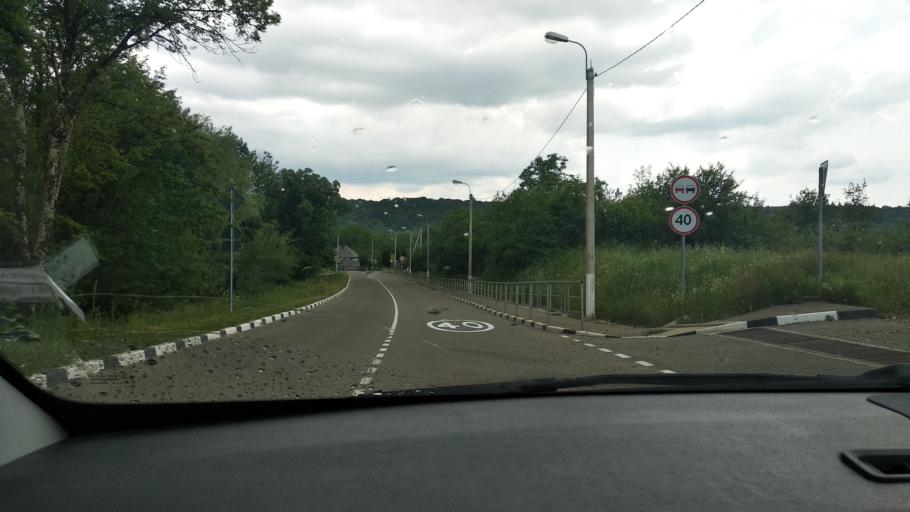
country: RU
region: Krasnodarskiy
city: Neftegorsk
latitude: 44.2726
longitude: 39.9259
